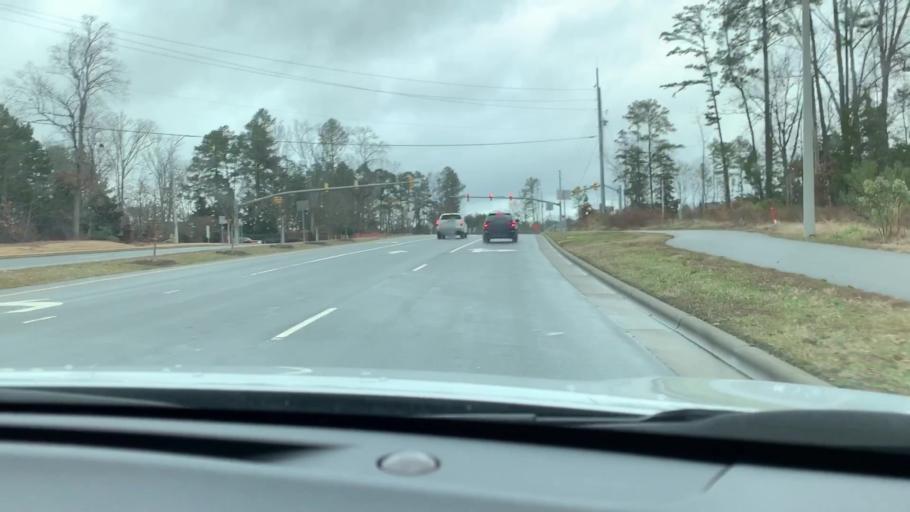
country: US
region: North Carolina
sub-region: Wake County
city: Green Level
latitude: 35.8283
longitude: -78.9007
